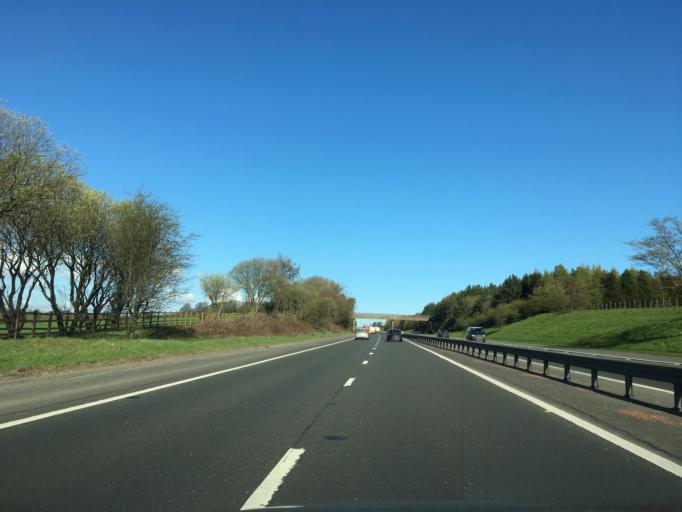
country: GB
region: Scotland
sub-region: West Lothian
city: Broxburn
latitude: 55.9744
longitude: -3.4696
